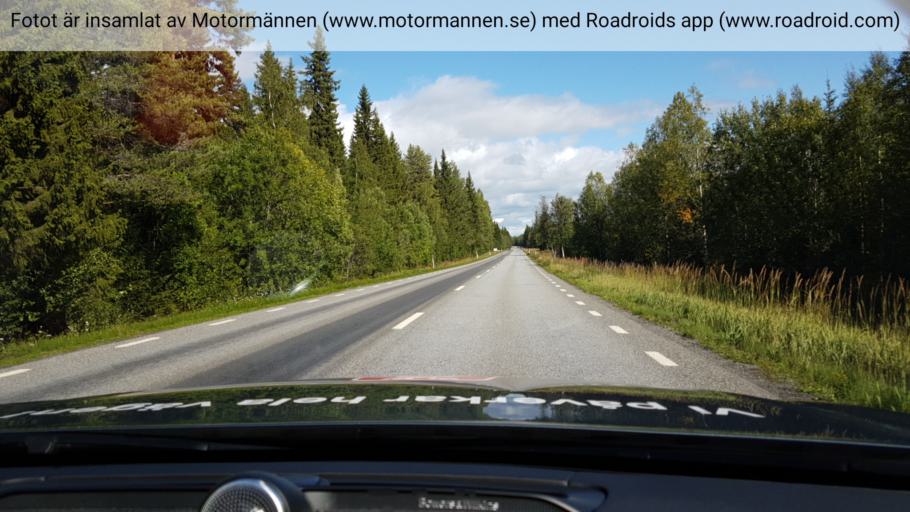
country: SE
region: Jaemtland
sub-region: Stroemsunds Kommun
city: Stroemsund
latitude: 63.5190
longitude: 15.2968
